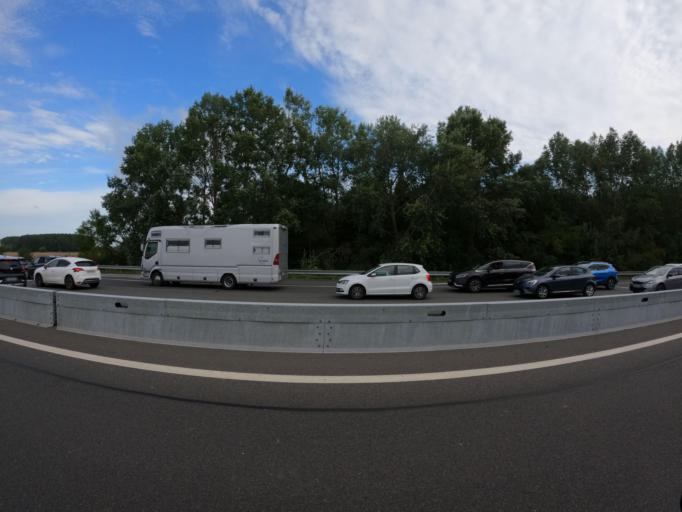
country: FR
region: Centre
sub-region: Departement d'Indre-et-Loire
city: Restigne
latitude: 47.2712
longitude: 0.2565
